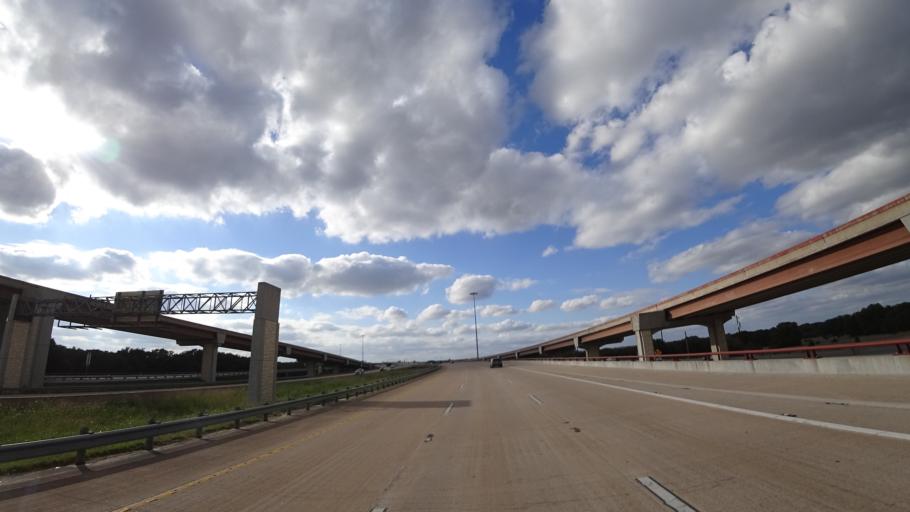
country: US
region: Texas
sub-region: Williamson County
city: Round Rock
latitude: 30.4792
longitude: -97.7118
